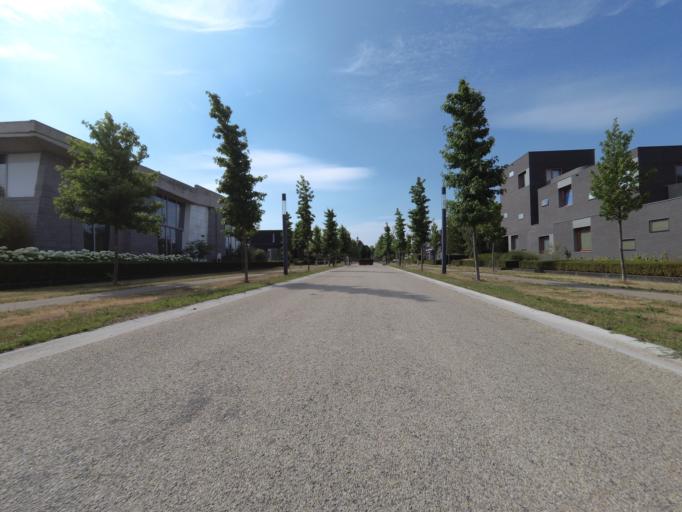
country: NL
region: Overijssel
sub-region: Gemeente Enschede
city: Enschede
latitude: 52.2298
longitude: 6.8958
